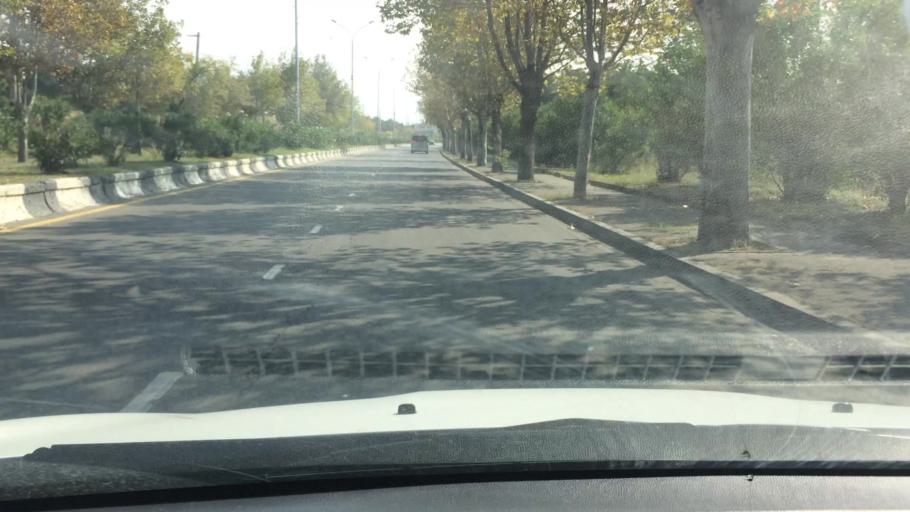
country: GE
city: Didi Lilo
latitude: 41.6797
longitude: 44.9579
